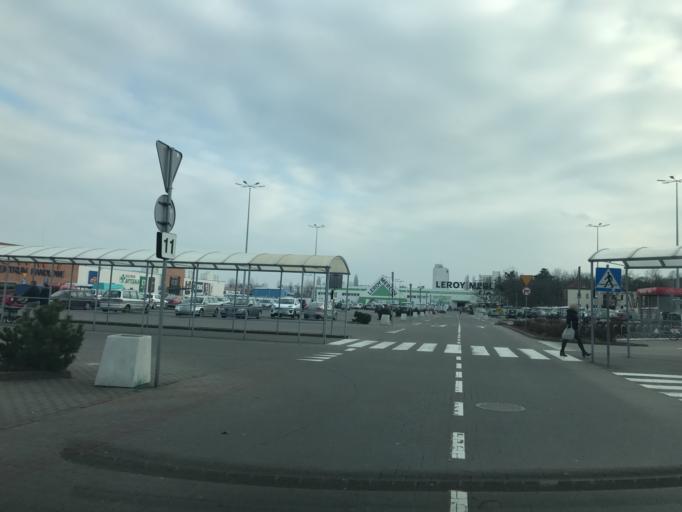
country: PL
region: Kujawsko-Pomorskie
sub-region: Powiat torunski
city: Lubicz Dolny
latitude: 53.0330
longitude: 18.6919
